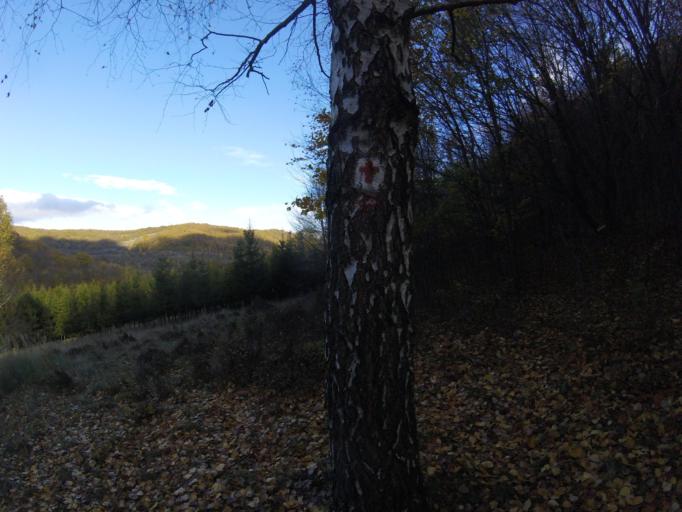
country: HU
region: Borsod-Abauj-Zemplen
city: Tolcsva
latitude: 48.3787
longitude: 21.3841
